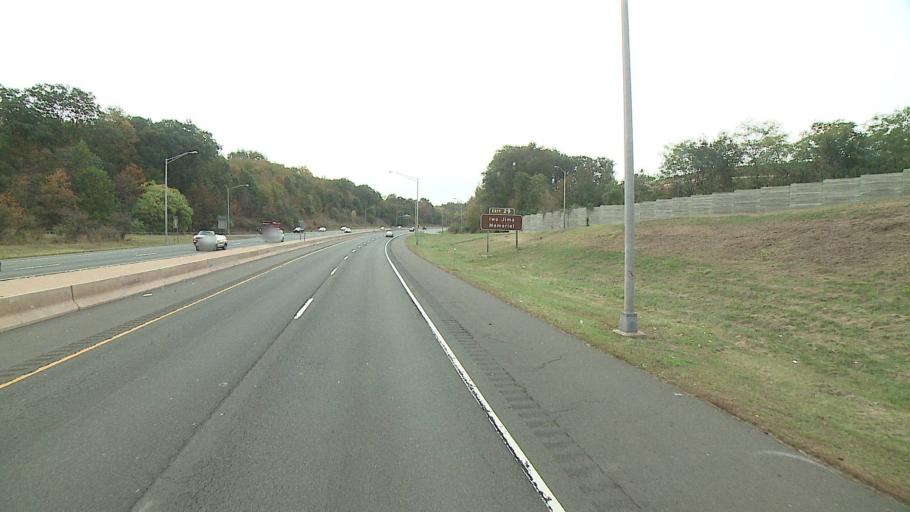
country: US
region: Connecticut
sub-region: Hartford County
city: Newington
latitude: 41.7123
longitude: -72.7630
